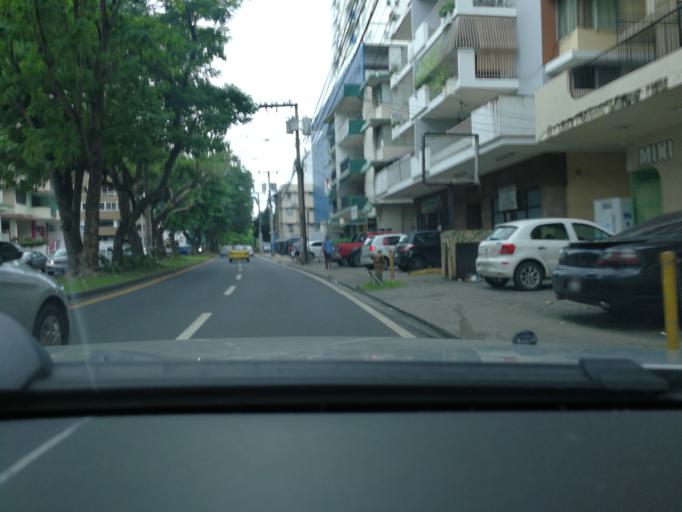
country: PA
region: Panama
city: Panama
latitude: 8.9935
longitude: -79.5239
